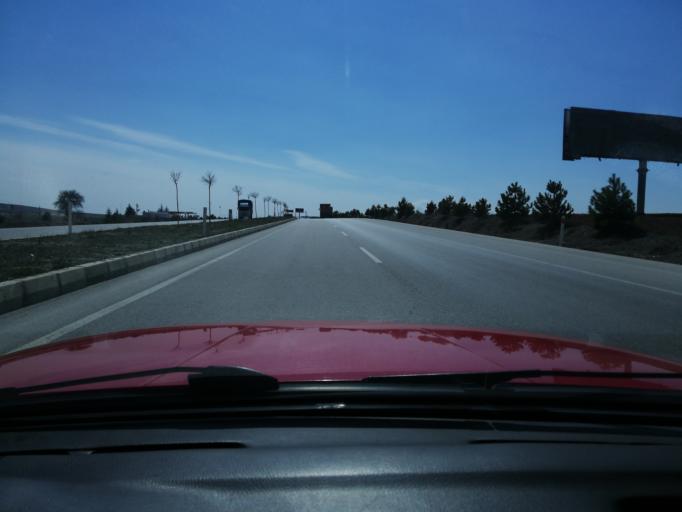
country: TR
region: Afyonkarahisar
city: Ihsaniye
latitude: 38.9052
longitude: 30.3789
